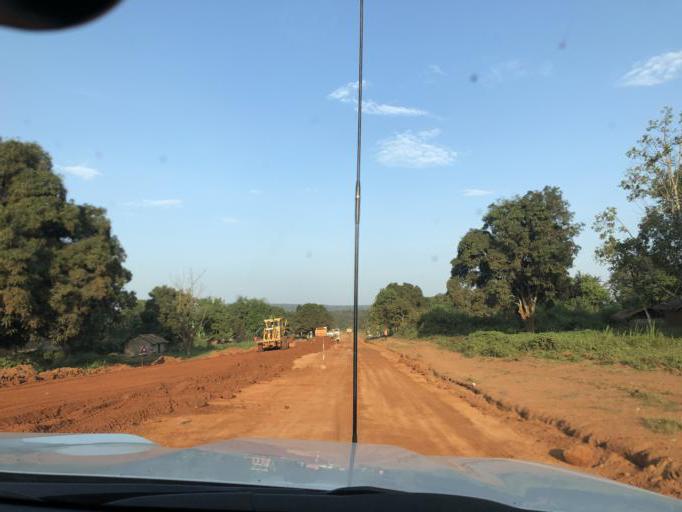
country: CF
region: Nana-Mambere
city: Bouar
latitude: 5.8935
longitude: 15.7518
